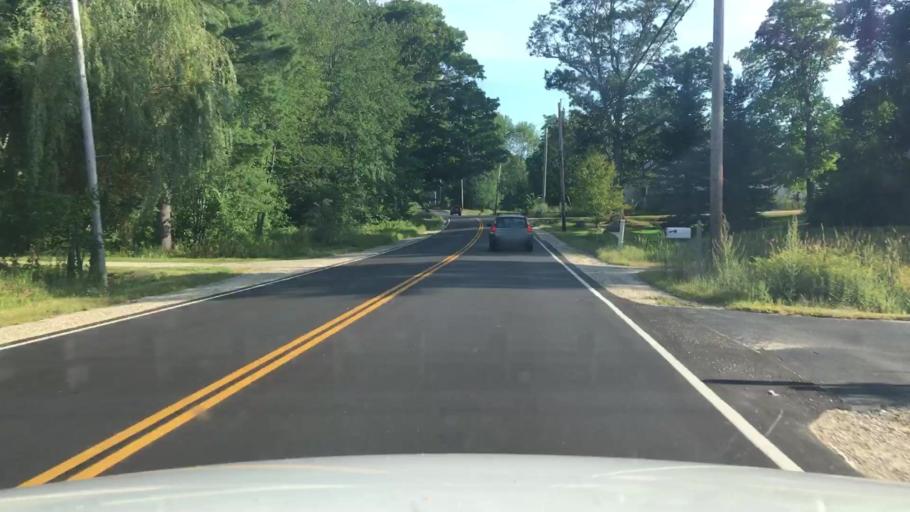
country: US
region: Maine
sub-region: Cumberland County
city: Cumberland Center
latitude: 43.7799
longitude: -70.3036
